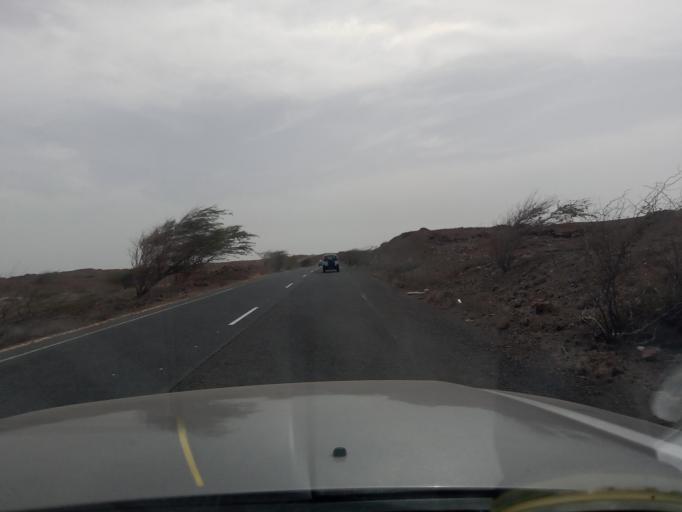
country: CV
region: Sal
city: Santa Maria
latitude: 16.6561
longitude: -22.9235
